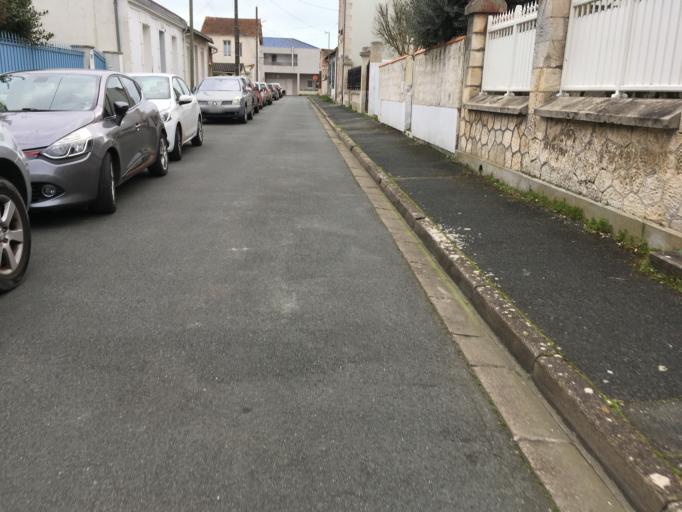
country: FR
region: Poitou-Charentes
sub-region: Departement de la Charente-Maritime
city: La Rochelle
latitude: 46.1674
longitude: -1.1624
